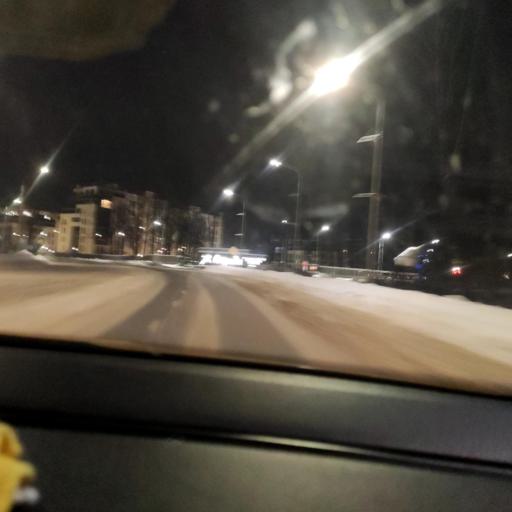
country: RU
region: Moskovskaya
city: Krasnogorsk
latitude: 55.8794
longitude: 37.3130
